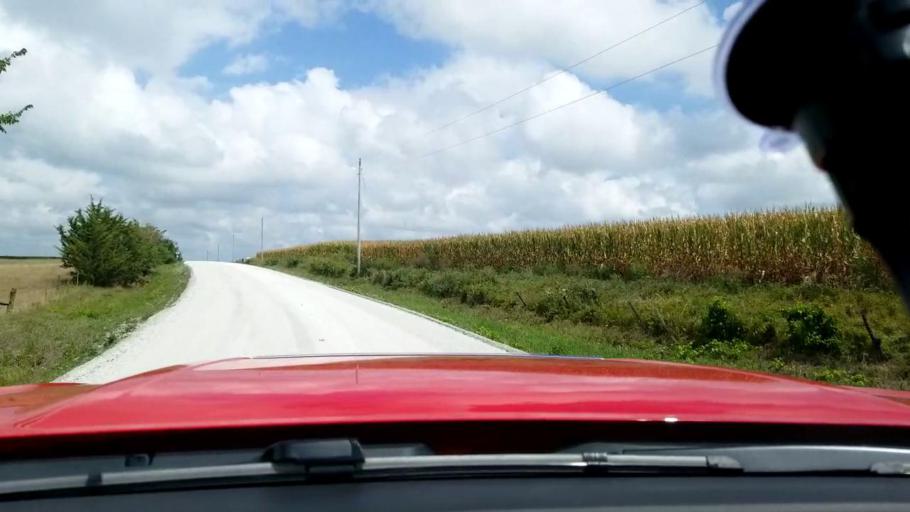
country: US
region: Iowa
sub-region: Decatur County
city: Lamoni
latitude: 40.6584
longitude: -94.0484
